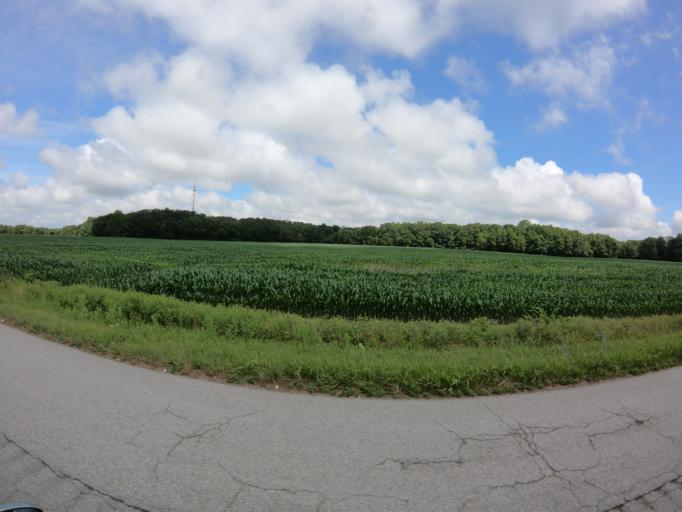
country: US
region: Maryland
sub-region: Queen Anne's County
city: Centreville
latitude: 39.0834
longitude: -75.9758
